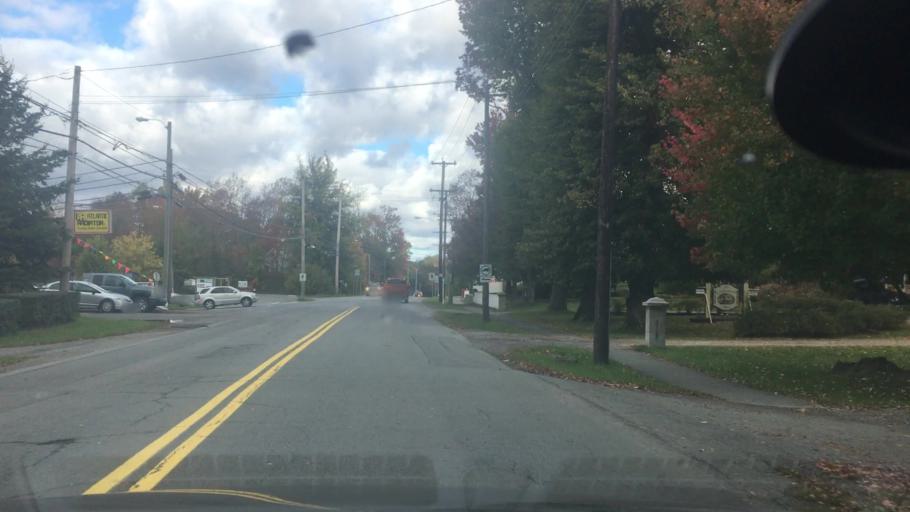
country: CA
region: Nova Scotia
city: Windsor
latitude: 44.9793
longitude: -64.1286
